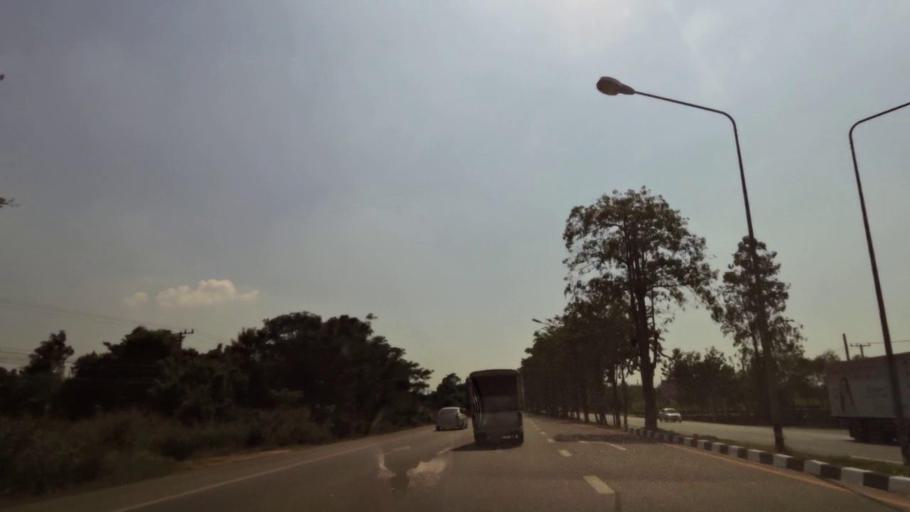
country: TH
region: Phichit
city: Bueng Na Rang
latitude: 16.1144
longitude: 100.1258
